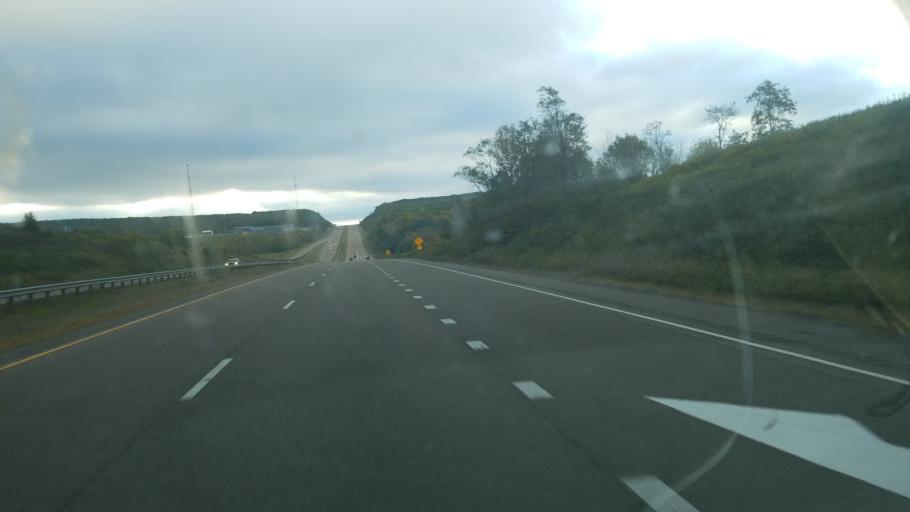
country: US
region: Pennsylvania
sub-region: Somerset County
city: Meyersdale
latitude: 39.6889
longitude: -79.1048
